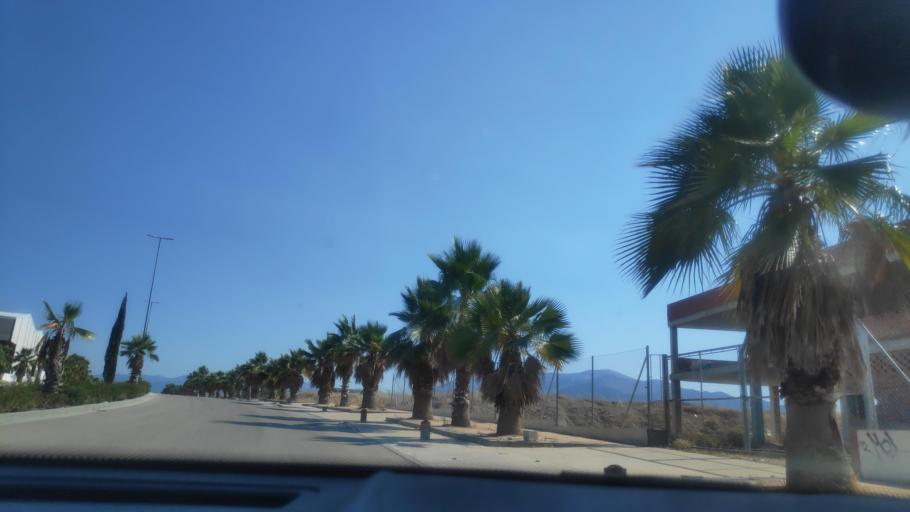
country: ES
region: Andalusia
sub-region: Provincia de Jaen
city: Jaen
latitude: 37.8262
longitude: -3.7763
